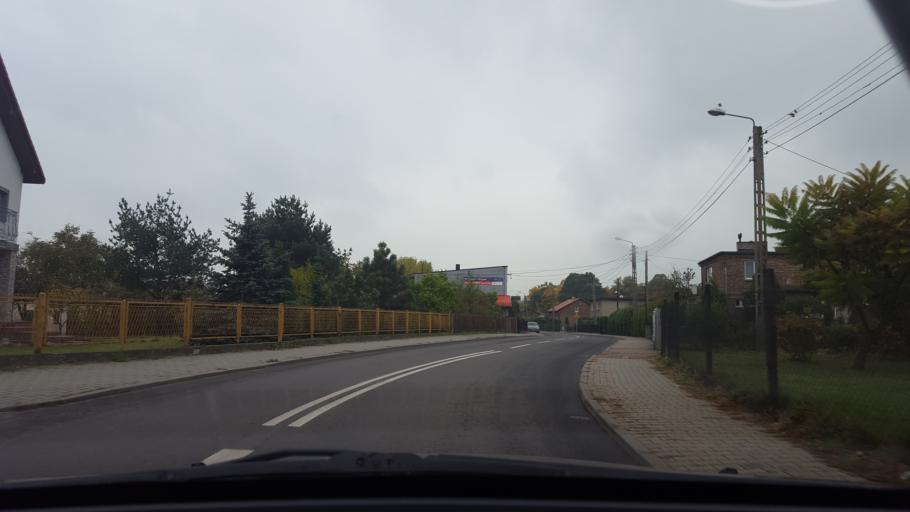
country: PL
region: Silesian Voivodeship
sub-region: Ruda Slaska
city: Ruda Slaska
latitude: 50.2349
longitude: 18.8636
